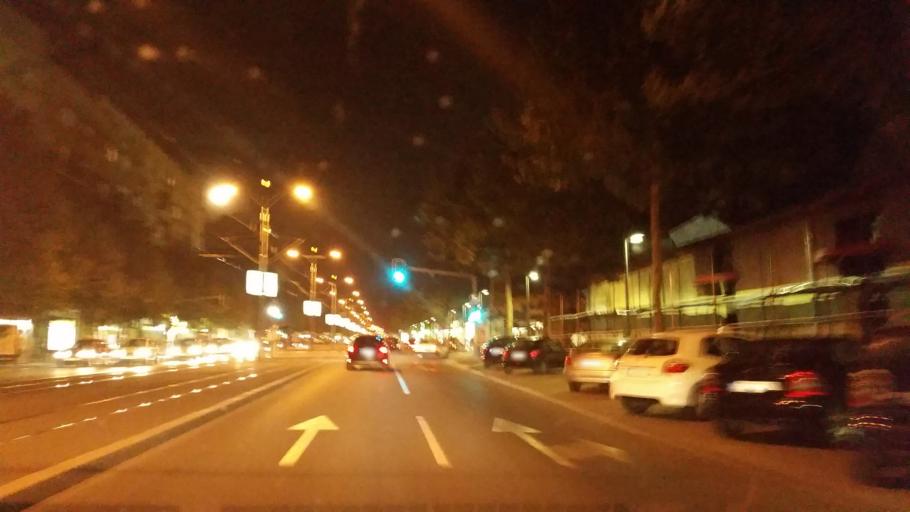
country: RS
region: Central Serbia
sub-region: Belgrade
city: Vracar
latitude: 44.8029
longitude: 20.4813
